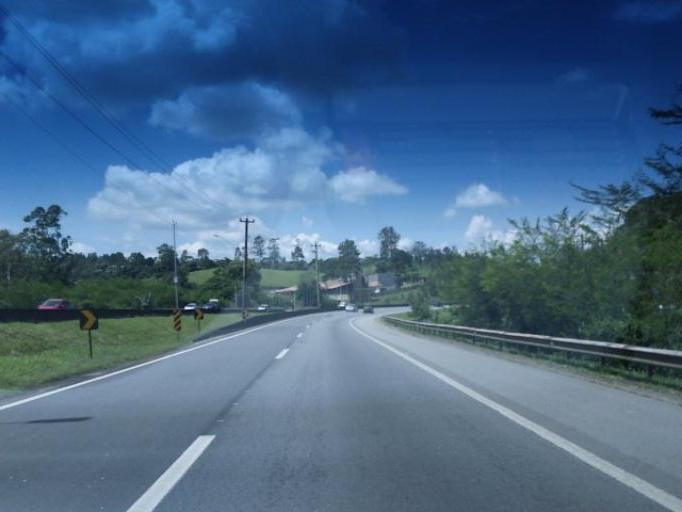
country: BR
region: Sao Paulo
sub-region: Sao Lourenco Da Serra
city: Sao Lourenco da Serra
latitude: -23.8546
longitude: -46.9401
